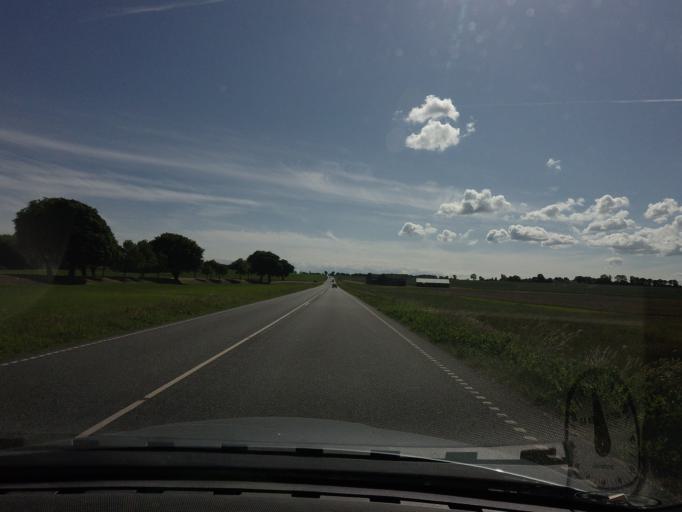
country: DK
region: Central Jutland
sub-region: Syddjurs Kommune
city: Ebeltoft
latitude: 56.3258
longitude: 10.7147
